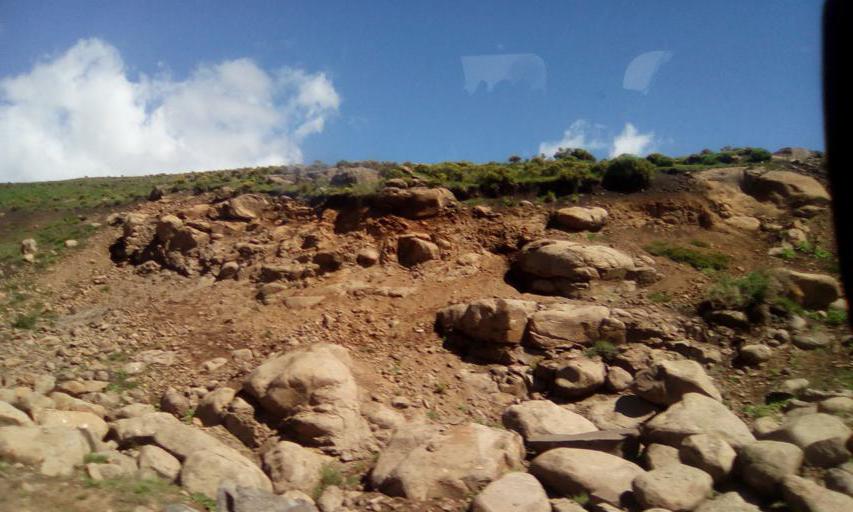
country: LS
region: Maseru
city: Nako
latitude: -29.8182
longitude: 28.0338
